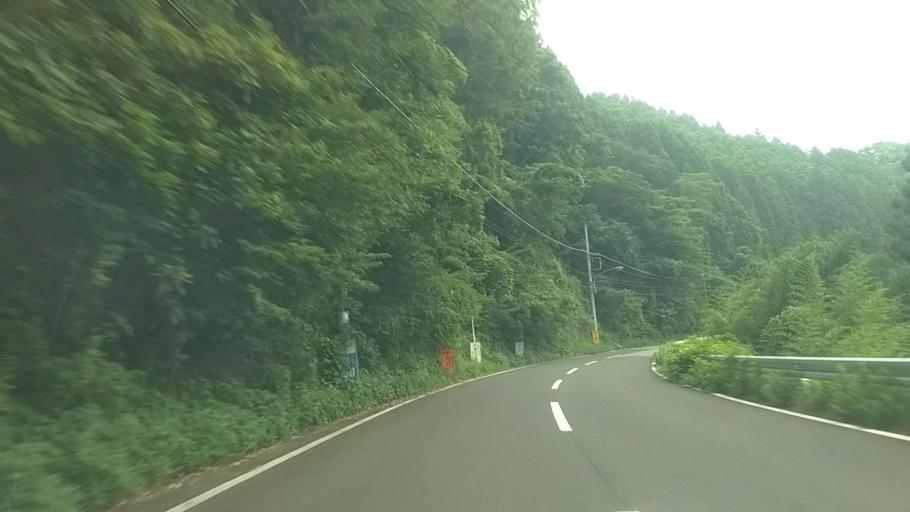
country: JP
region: Chiba
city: Katsuura
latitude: 35.2460
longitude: 140.2407
